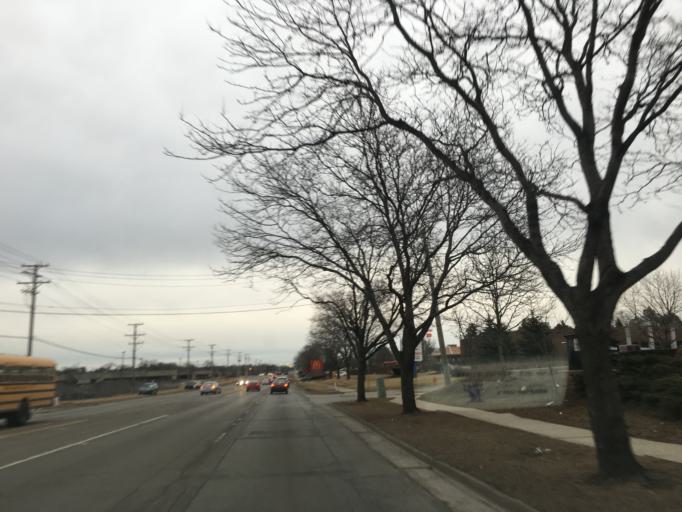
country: US
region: Illinois
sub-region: Cook County
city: Hoffman Estates
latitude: 42.0740
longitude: -88.0617
